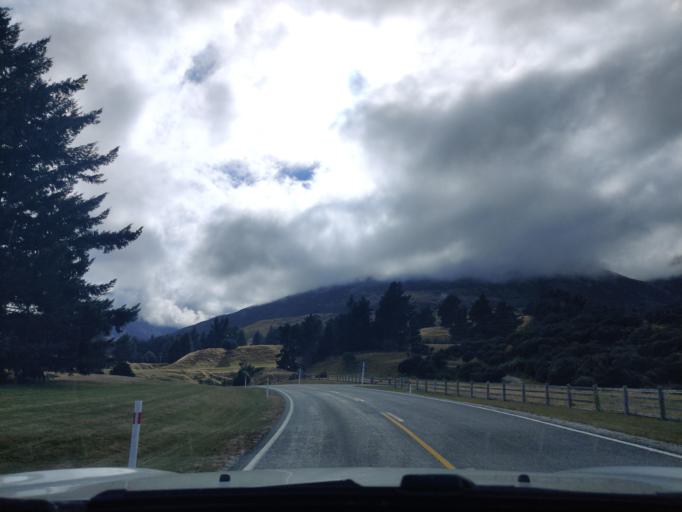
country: NZ
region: Otago
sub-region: Queenstown-Lakes District
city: Queenstown
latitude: -44.8707
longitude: 168.4025
